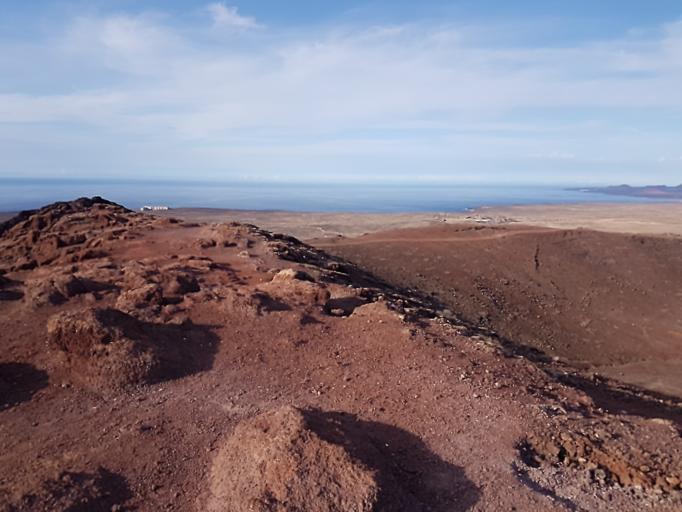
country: ES
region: Canary Islands
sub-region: Provincia de Las Palmas
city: Playa Blanca
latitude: 28.8686
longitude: -13.8578
